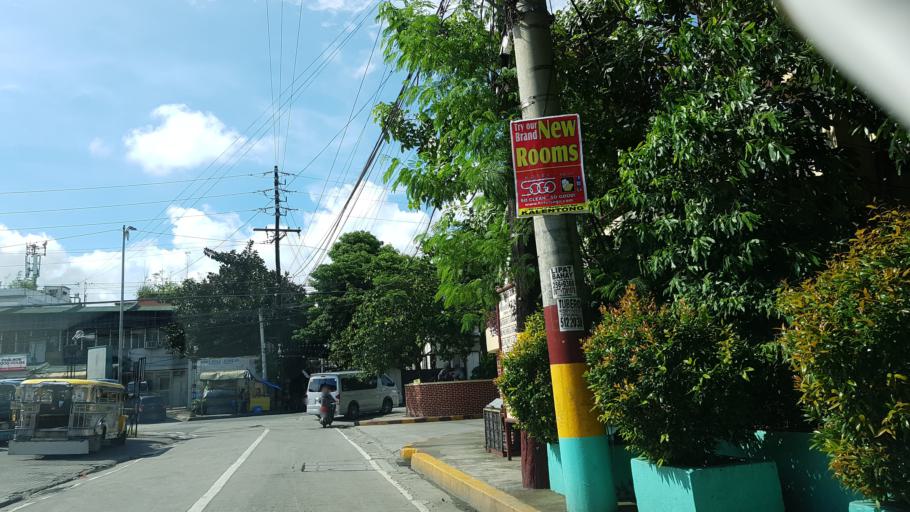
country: PH
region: Metro Manila
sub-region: San Juan
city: San Juan
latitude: 14.5844
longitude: 121.0181
